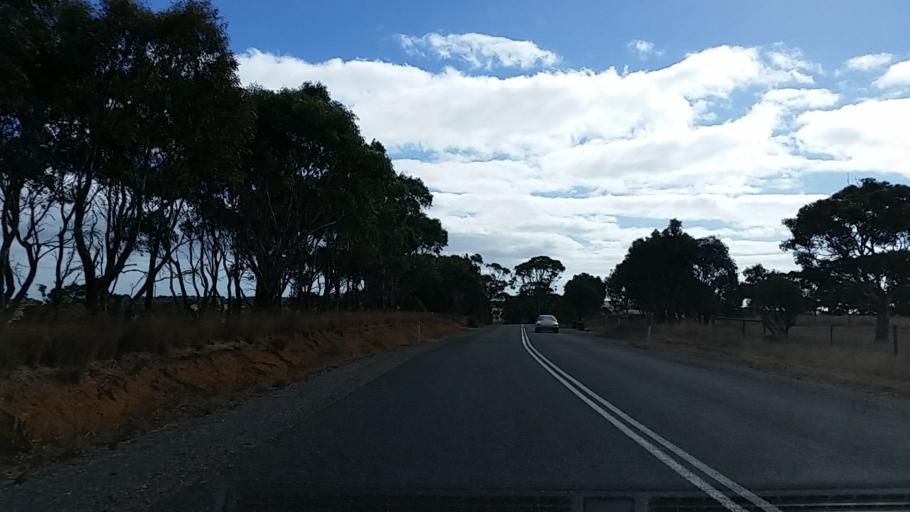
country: AU
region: South Australia
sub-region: Yankalilla
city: Normanville
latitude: -35.4109
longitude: 138.3958
